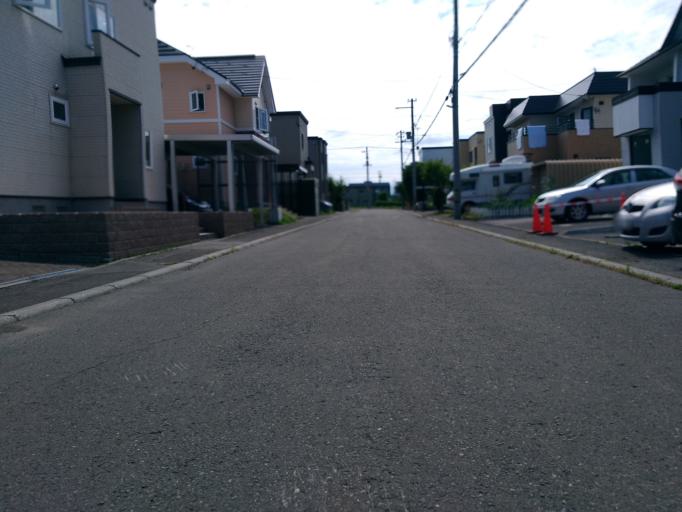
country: JP
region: Hokkaido
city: Ebetsu
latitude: 43.0833
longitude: 141.5204
